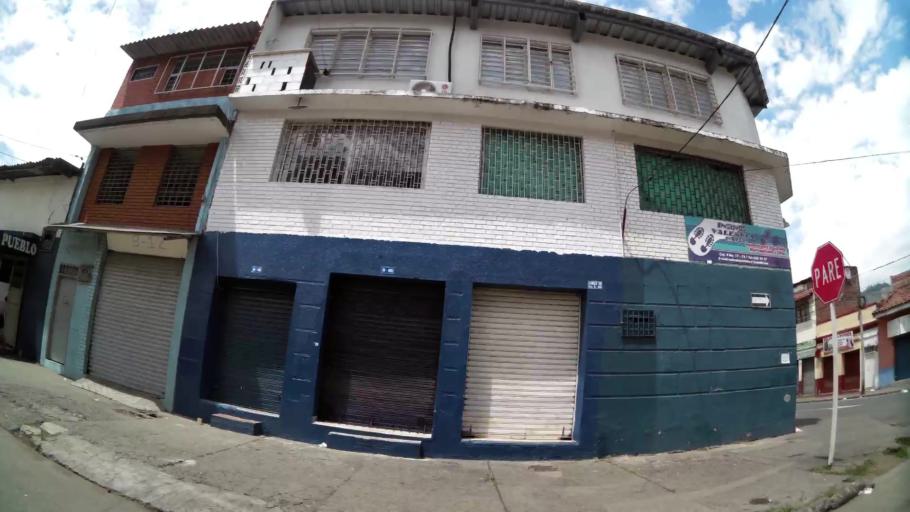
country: CO
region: Valle del Cauca
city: Cali
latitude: 3.4494
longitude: -76.5253
